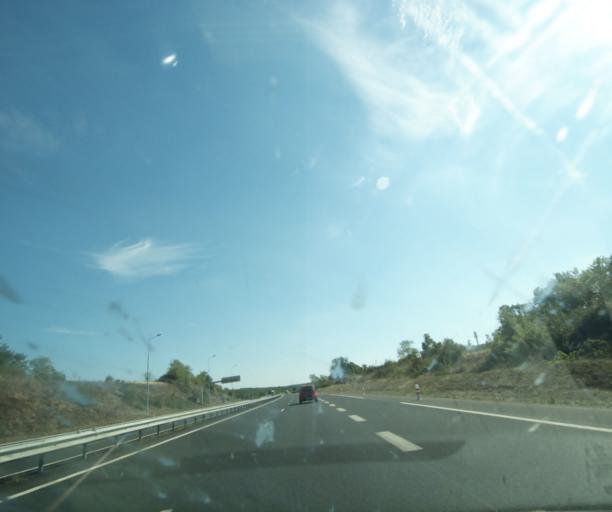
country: FR
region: Limousin
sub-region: Departement de la Correze
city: Cosnac
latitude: 45.0278
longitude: 1.5294
